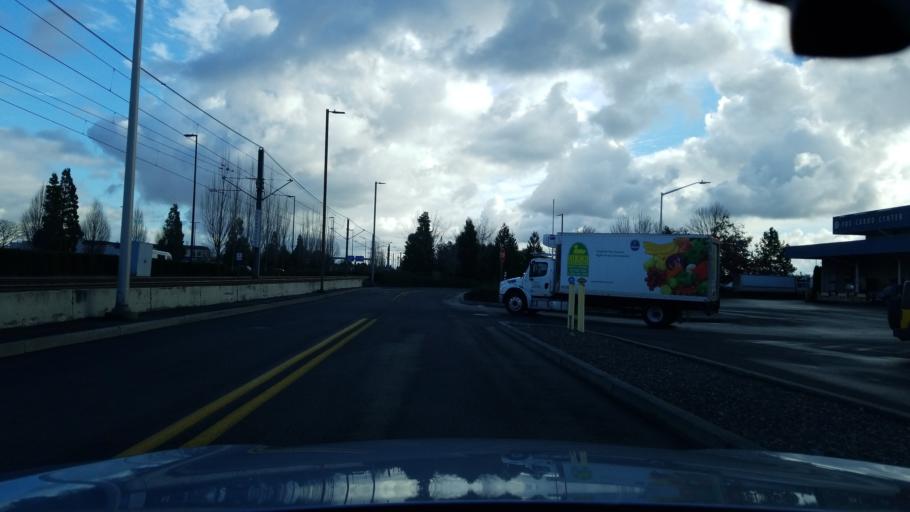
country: US
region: Washington
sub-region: Clark County
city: Orchards
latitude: 45.5831
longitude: -122.5788
